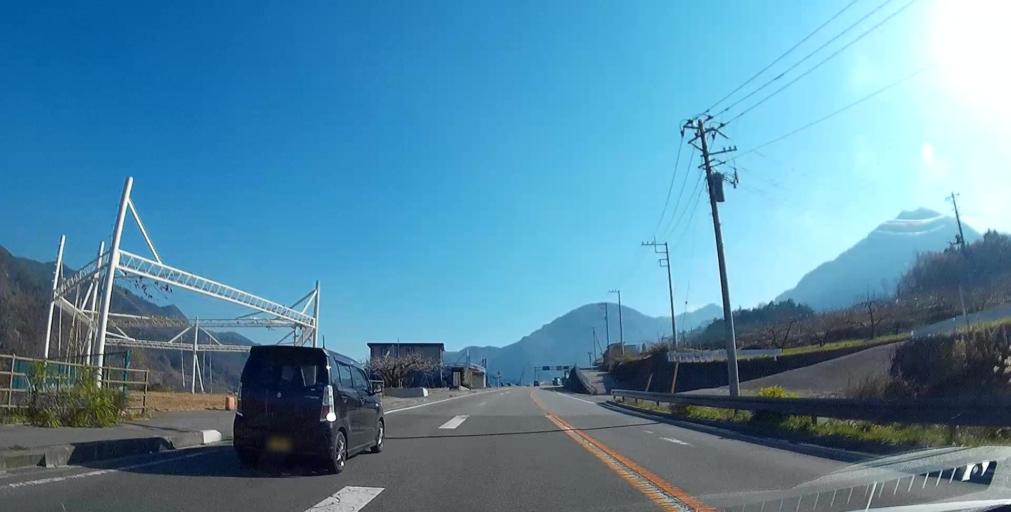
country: JP
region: Yamanashi
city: Isawa
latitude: 35.6099
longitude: 138.7004
